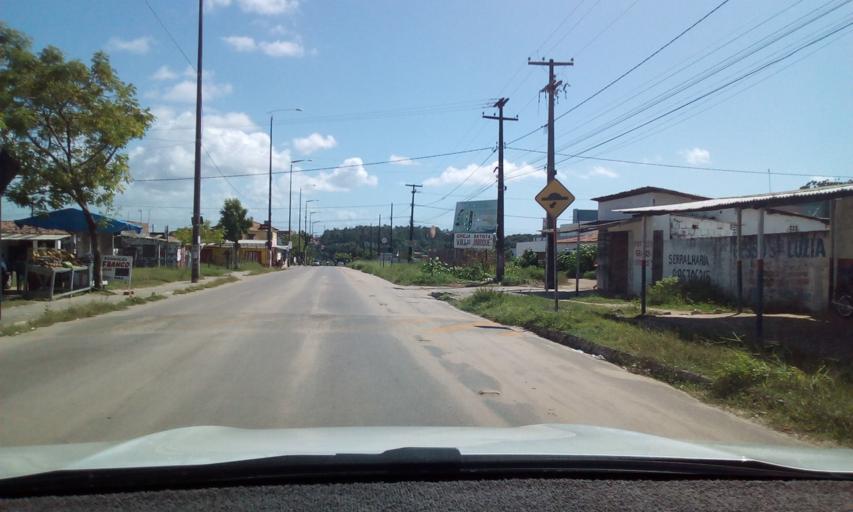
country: BR
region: Paraiba
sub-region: Joao Pessoa
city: Joao Pessoa
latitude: -7.1984
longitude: -34.8342
